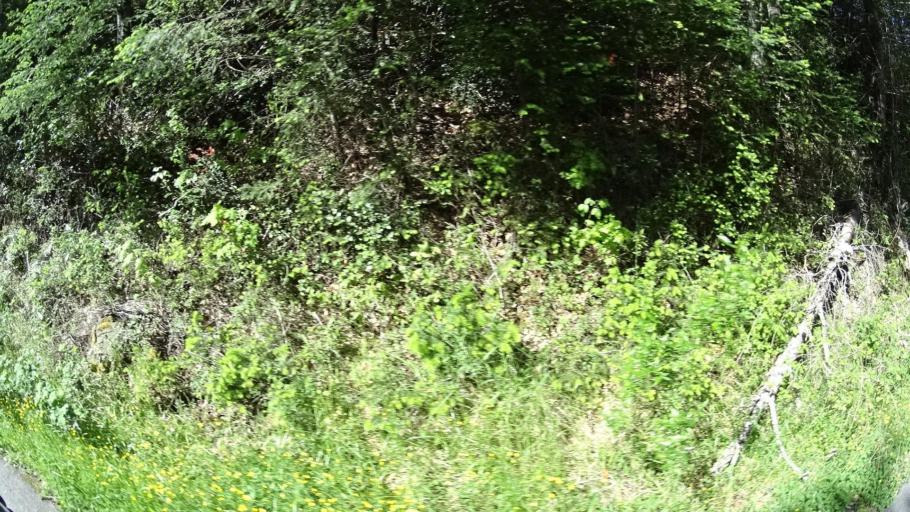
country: US
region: California
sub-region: Humboldt County
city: Rio Dell
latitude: 40.2302
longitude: -124.1105
